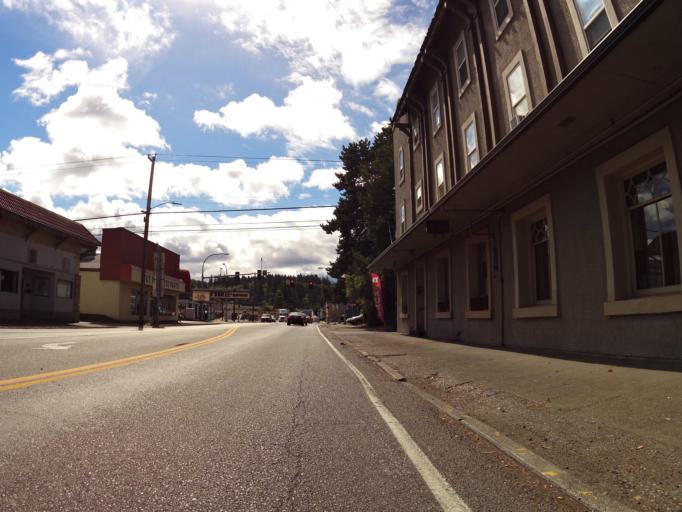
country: US
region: Washington
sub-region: Mason County
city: Shelton
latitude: 47.2127
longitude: -123.1002
